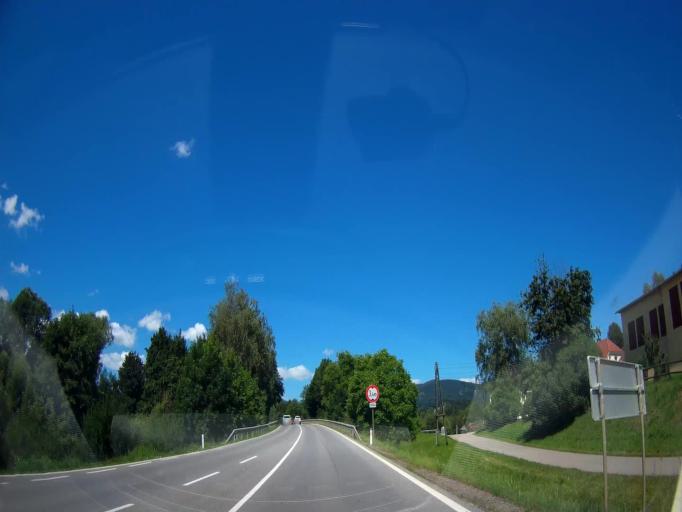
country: AT
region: Carinthia
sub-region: Politischer Bezirk Sankt Veit an der Glan
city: Sankt Veit an der Glan
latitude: 46.7653
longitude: 14.3822
